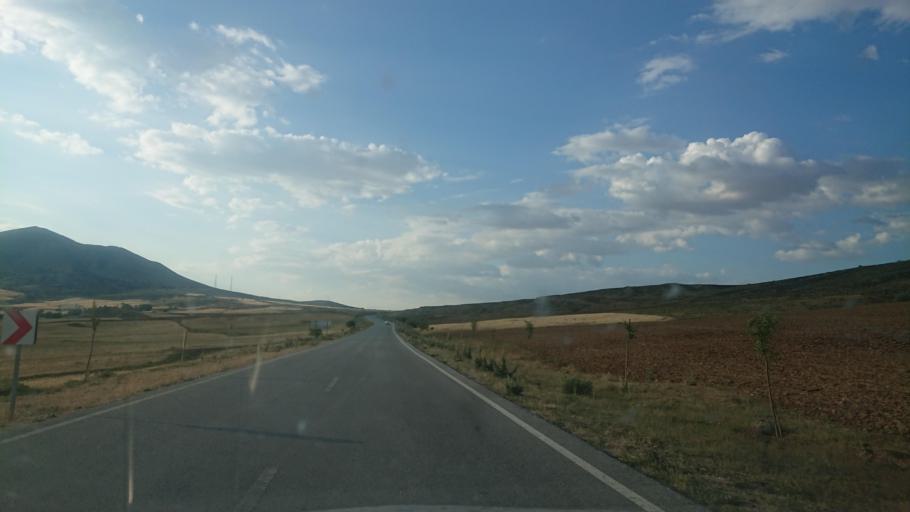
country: TR
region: Aksaray
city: Balci
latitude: 38.6023
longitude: 34.1029
